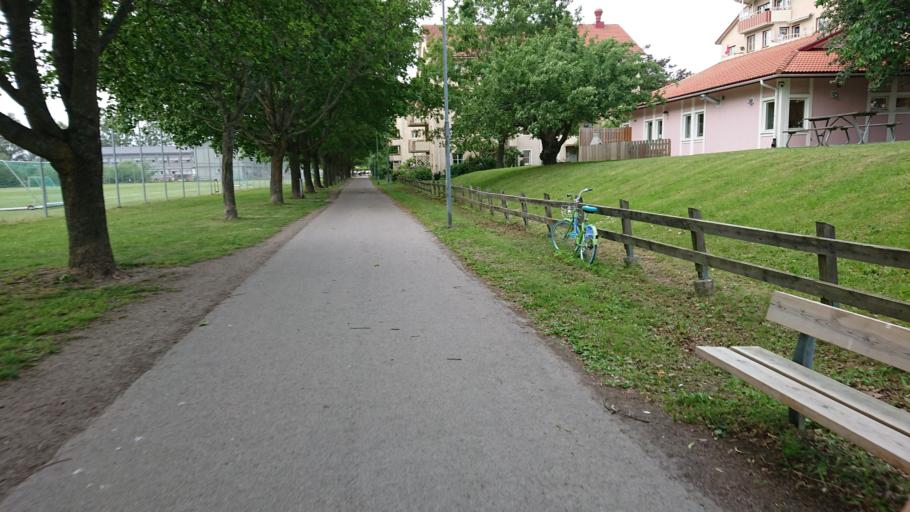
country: SE
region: Uppsala
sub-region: Uppsala Kommun
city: Uppsala
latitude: 59.8731
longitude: 17.6192
